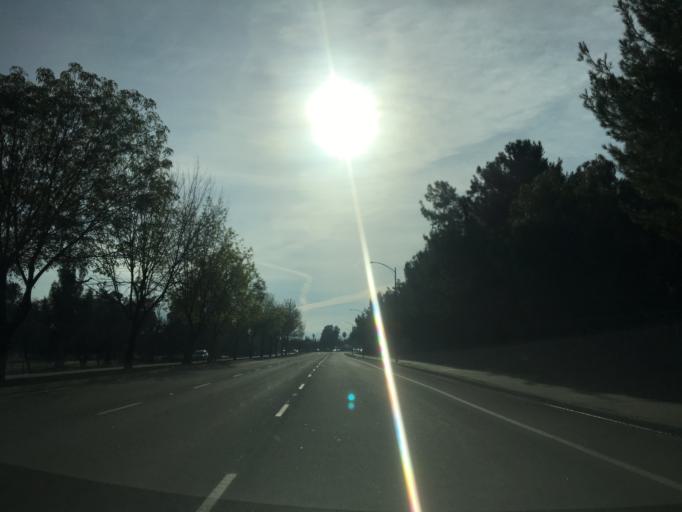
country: US
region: California
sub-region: Santa Clara County
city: Alum Rock
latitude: 37.3380
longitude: -121.8029
